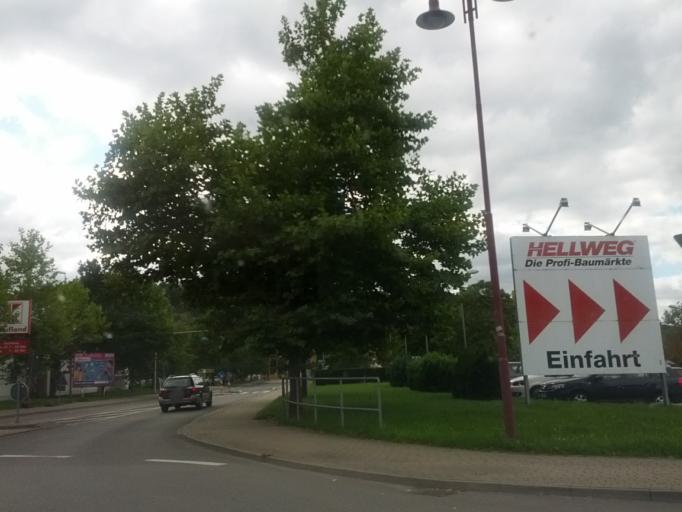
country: DE
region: Thuringia
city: Schmalkalden
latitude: 50.7231
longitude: 10.4471
